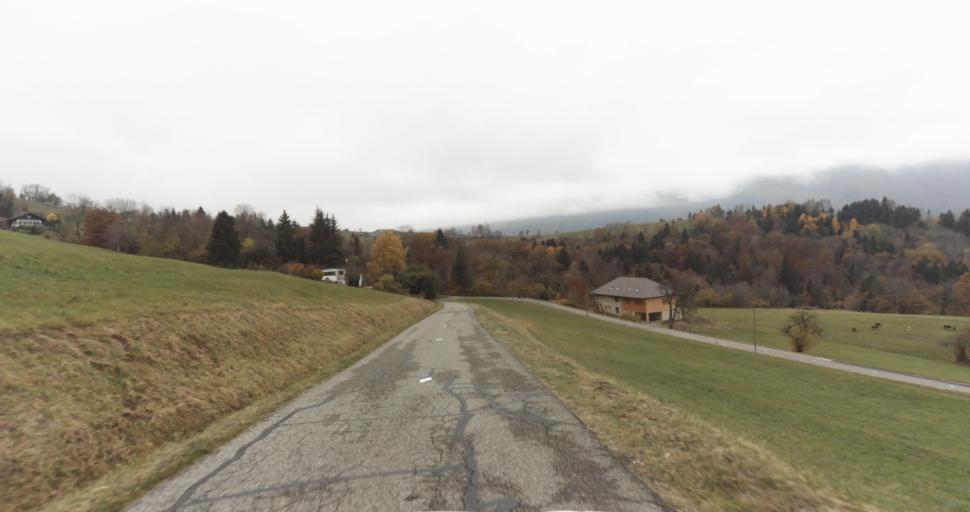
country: FR
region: Rhone-Alpes
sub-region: Departement de la Haute-Savoie
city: Saint-Jorioz
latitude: 45.8132
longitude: 6.1686
